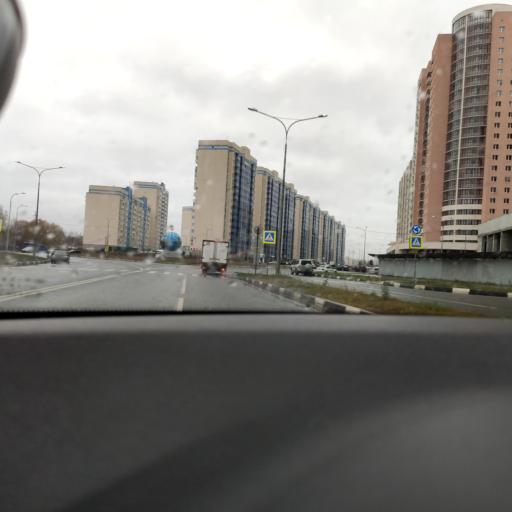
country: RU
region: Samara
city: Rozhdestveno
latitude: 53.1476
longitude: 50.0749
